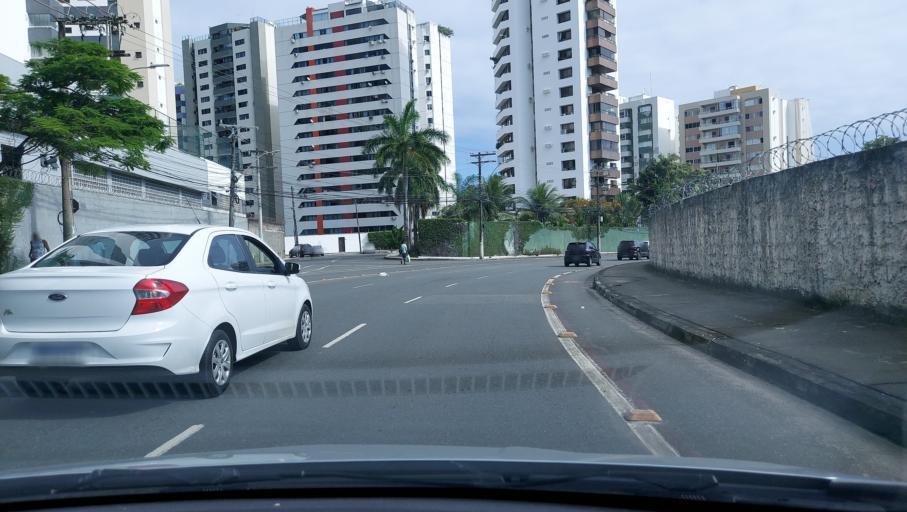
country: BR
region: Bahia
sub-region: Salvador
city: Salvador
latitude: -12.9878
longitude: -38.4635
